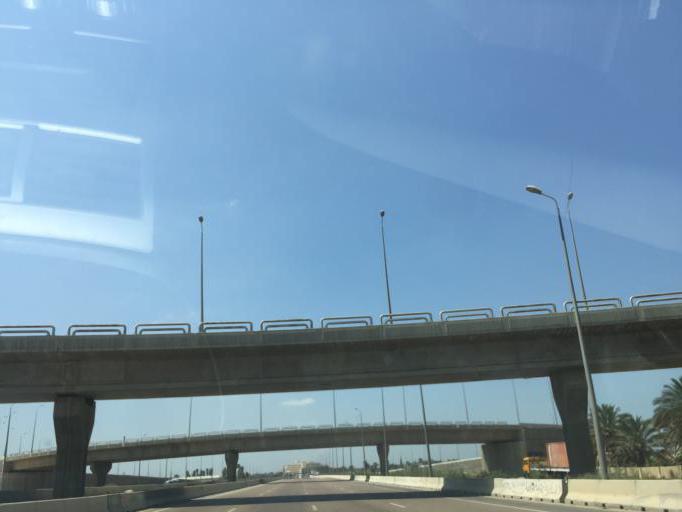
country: EG
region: Al Buhayrah
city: Abu al Matamir
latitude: 30.8886
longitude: 29.8801
